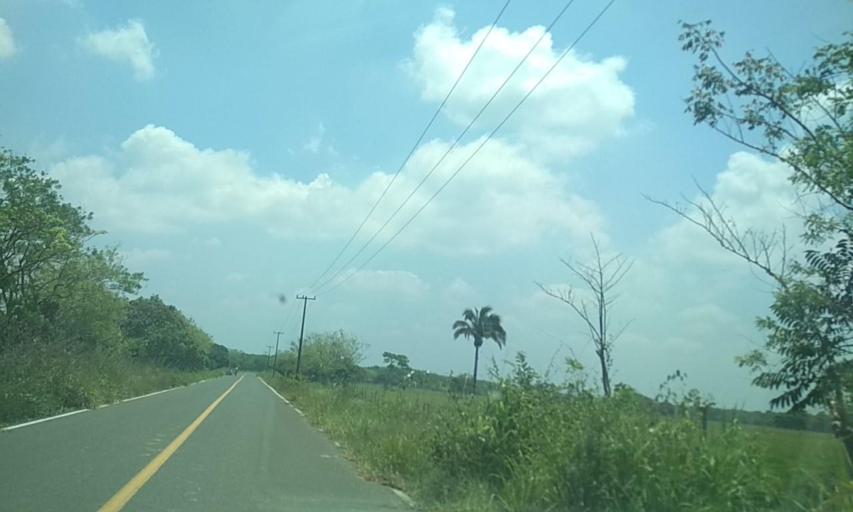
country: MX
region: Tabasco
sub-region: Huimanguillo
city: Francisco Rueda
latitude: 17.7581
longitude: -94.0546
